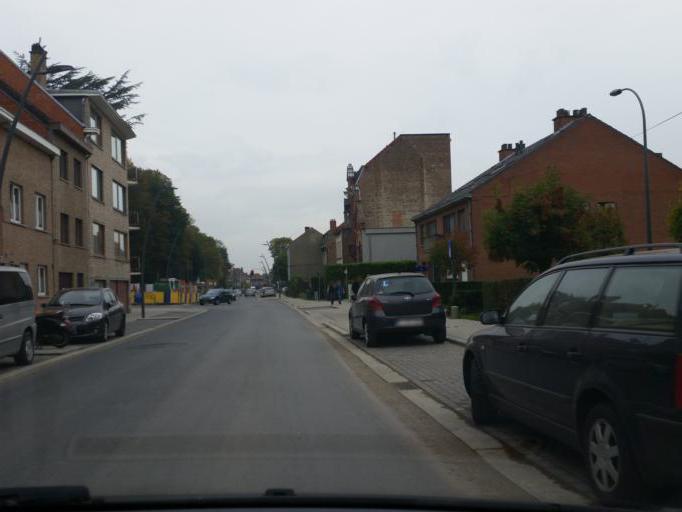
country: BE
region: Flanders
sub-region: Provincie Vlaams-Brabant
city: Drogenbos
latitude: 50.7834
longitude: 4.3197
